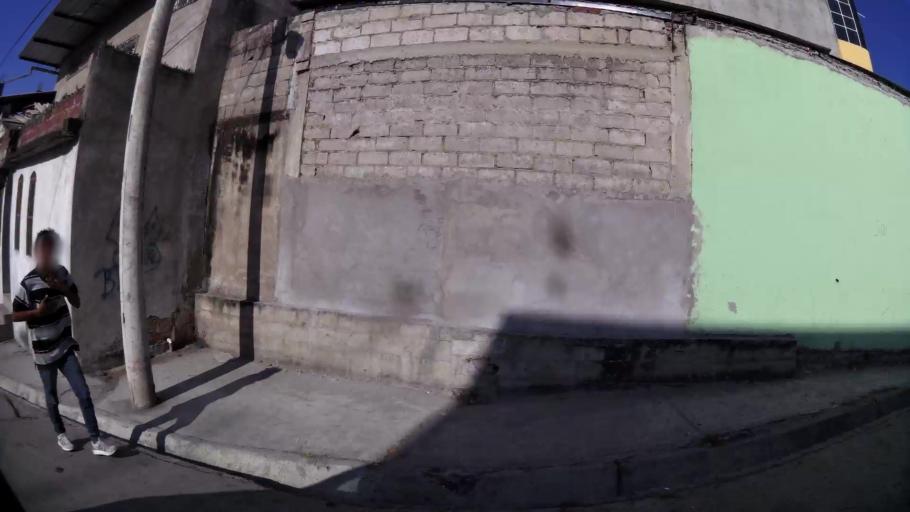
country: EC
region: Guayas
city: Guayaquil
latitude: -2.1551
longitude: -79.9146
